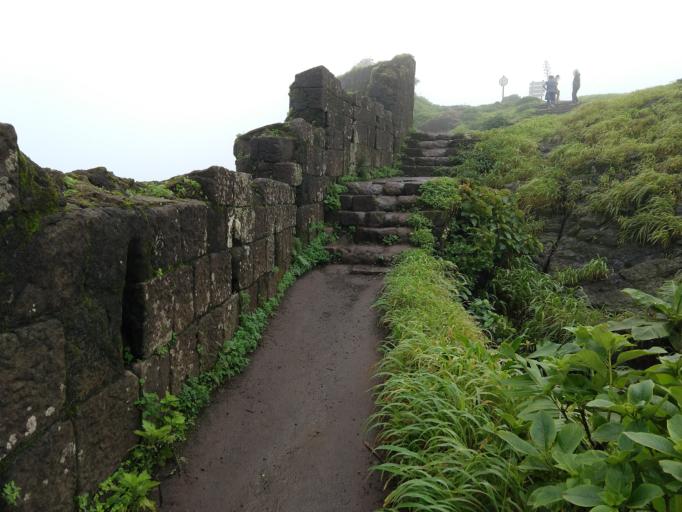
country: IN
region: Maharashtra
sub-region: Pune Division
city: Kharakvasla
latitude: 18.3657
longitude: 73.7528
